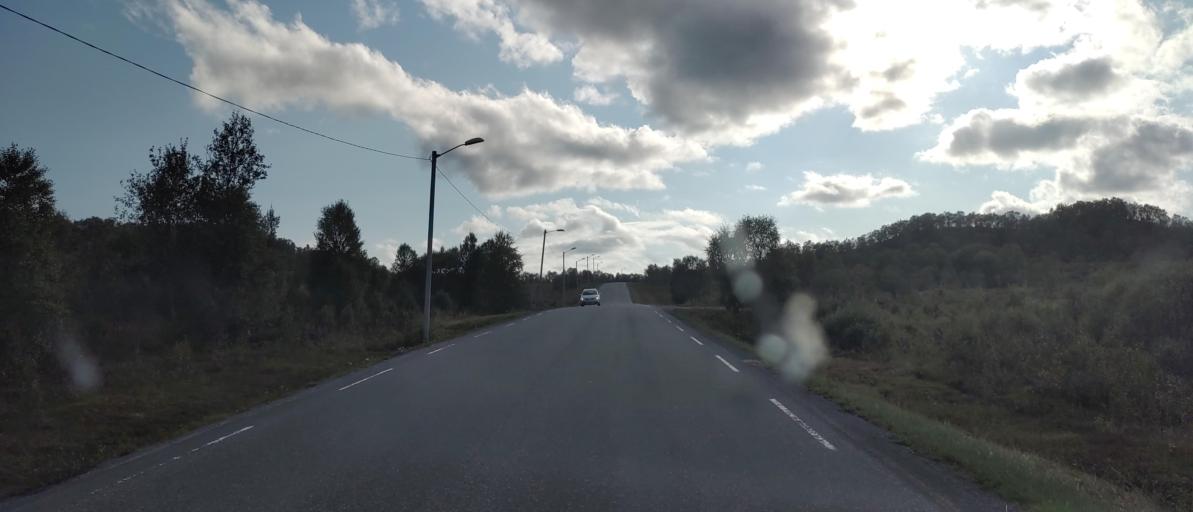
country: NO
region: Nordland
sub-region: Sortland
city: Sortland
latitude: 68.7225
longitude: 15.4686
